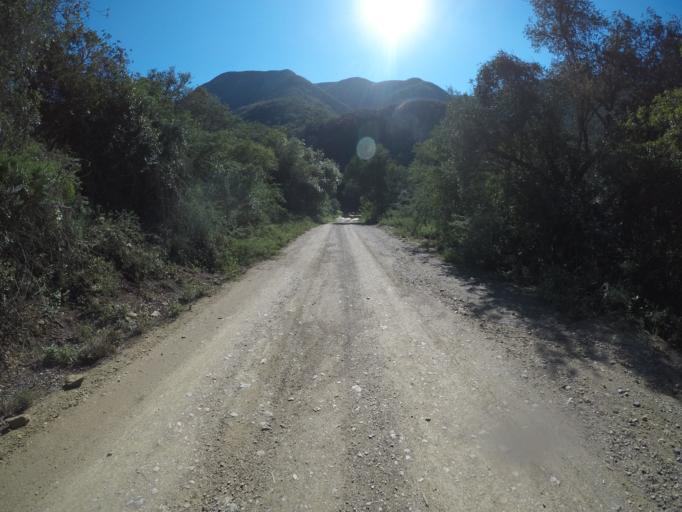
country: ZA
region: Eastern Cape
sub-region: Cacadu District Municipality
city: Kareedouw
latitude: -33.6575
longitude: 24.5262
